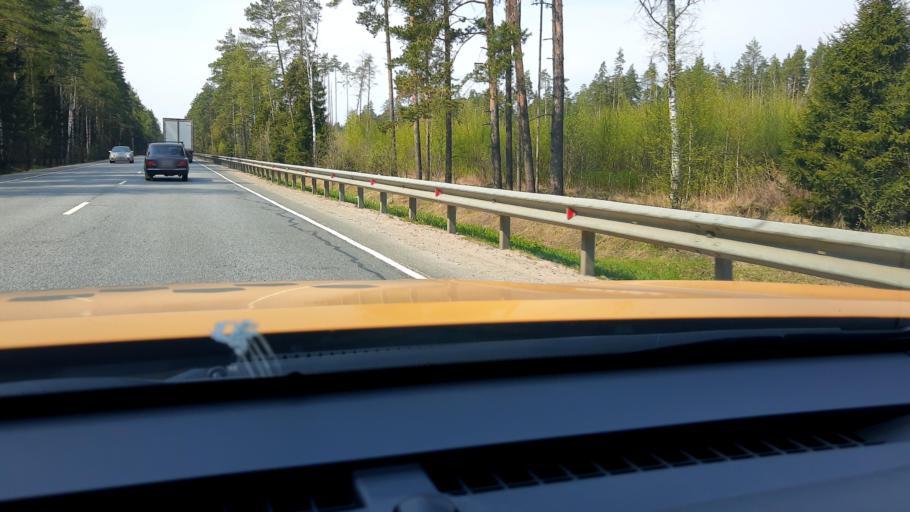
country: RU
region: Moskovskaya
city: Chernogolovka
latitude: 56.0182
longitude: 38.2477
